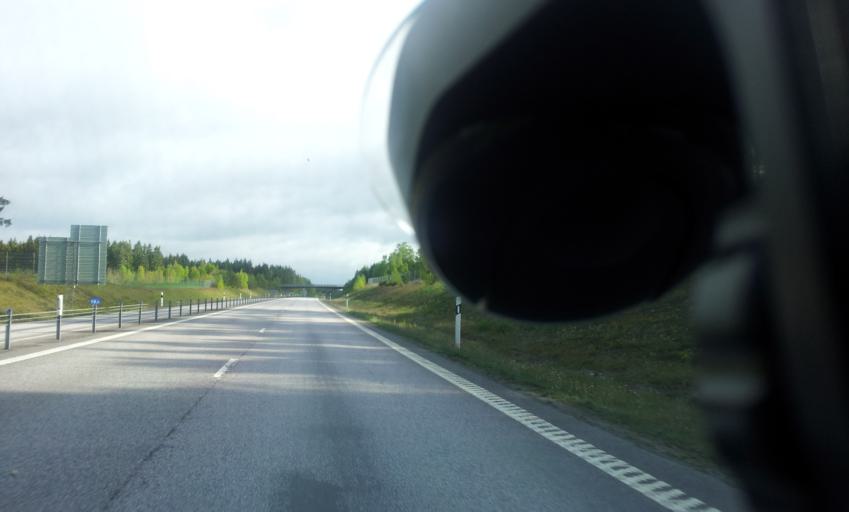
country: SE
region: Kalmar
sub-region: Torsas Kommun
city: Torsas
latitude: 56.4597
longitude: 16.0785
